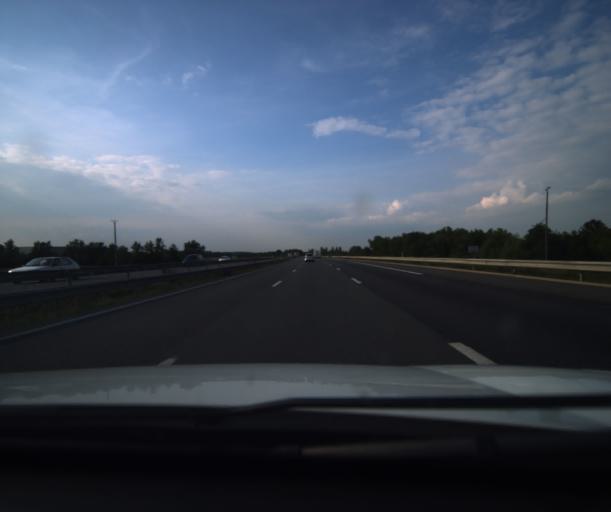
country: FR
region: Midi-Pyrenees
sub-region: Departement du Tarn-et-Garonne
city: Campsas
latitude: 43.9129
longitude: 1.3193
